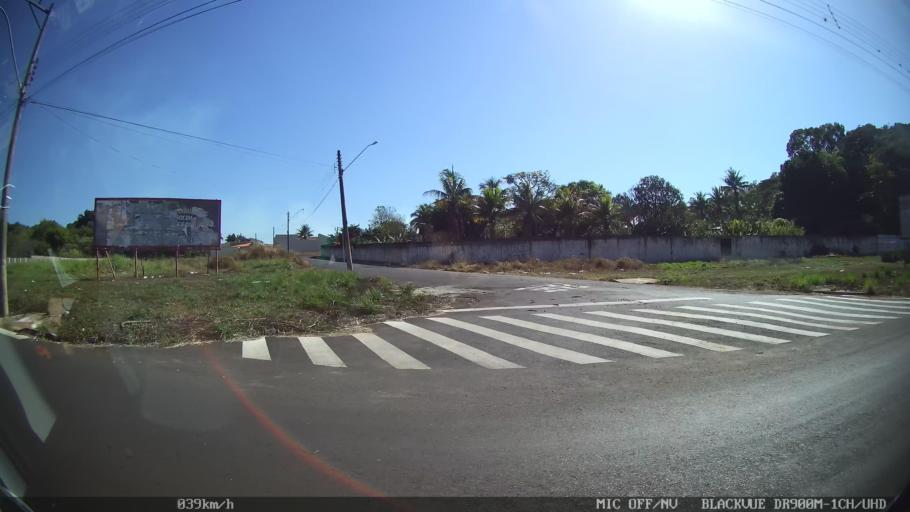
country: BR
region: Sao Paulo
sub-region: Batatais
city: Batatais
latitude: -20.8818
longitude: -47.5923
